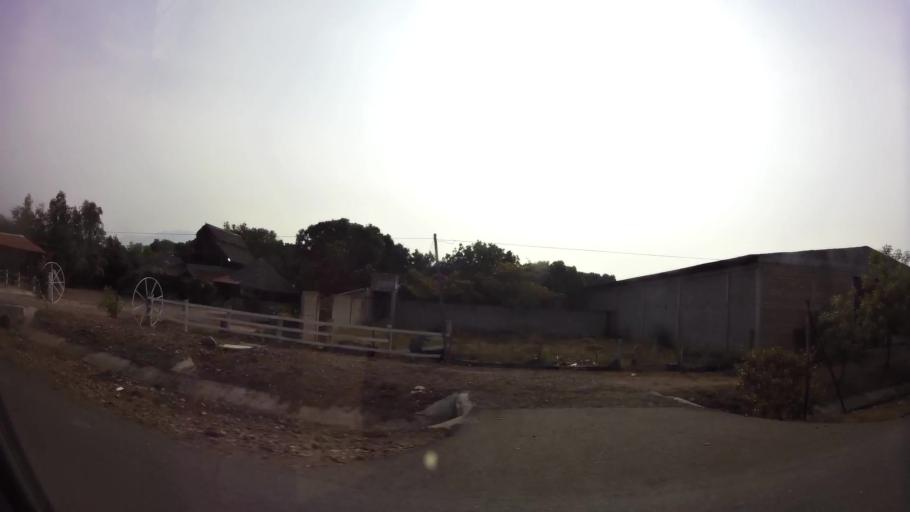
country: HN
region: La Paz
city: Yarumela
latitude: 14.3741
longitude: -87.6067
